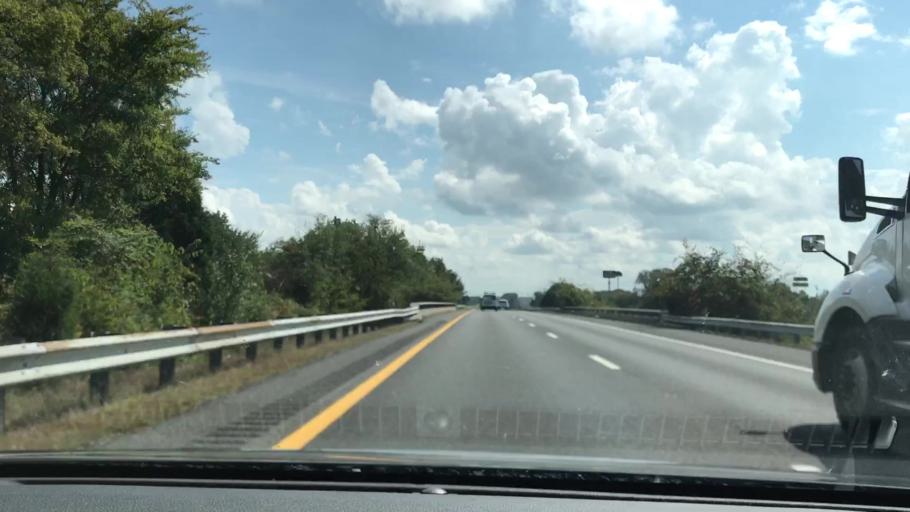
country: US
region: Tennessee
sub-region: Montgomery County
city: Clarksville
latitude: 36.6002
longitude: -87.2832
